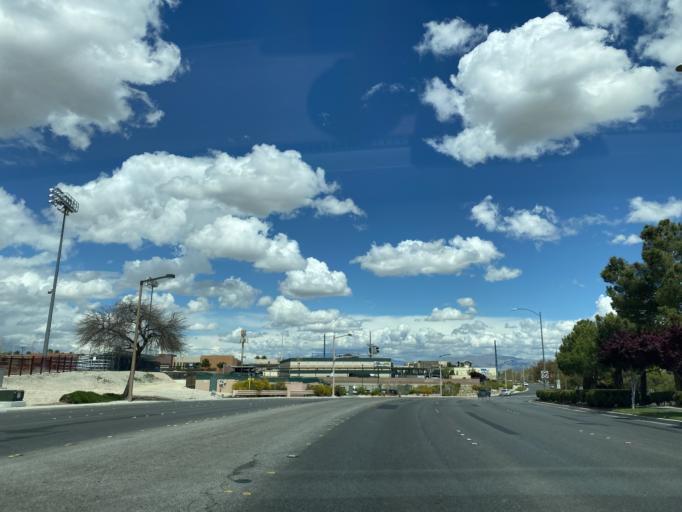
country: US
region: Nevada
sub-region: Clark County
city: Summerlin South
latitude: 36.1554
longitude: -115.3161
